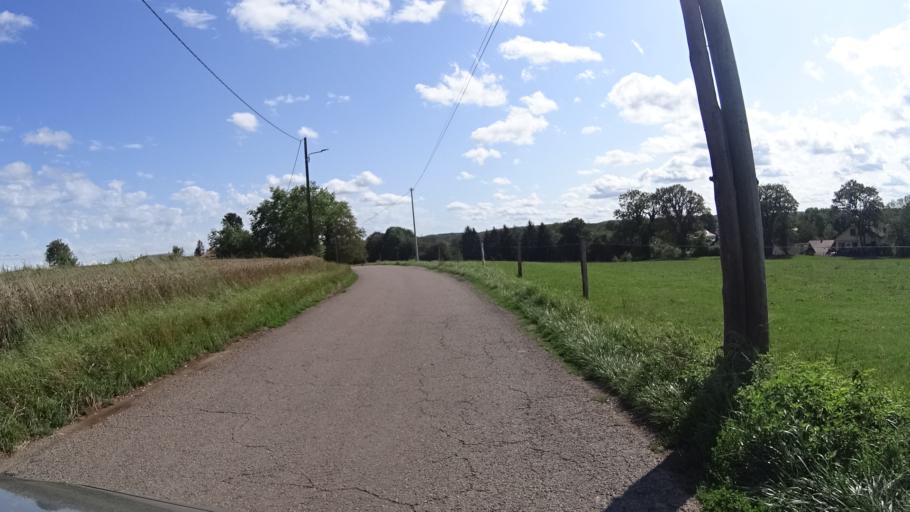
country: FR
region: Franche-Comte
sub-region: Departement du Doubs
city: Saone
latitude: 47.2156
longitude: 6.1117
